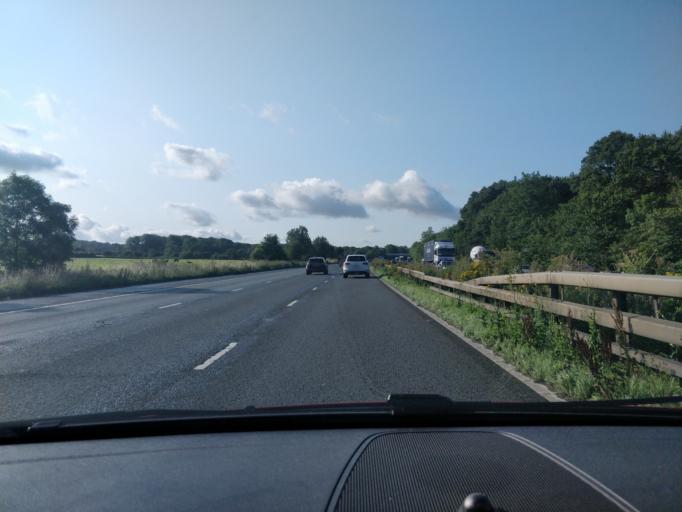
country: GB
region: England
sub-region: Knowsley
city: Knowsley
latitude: 53.4505
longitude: -2.8635
